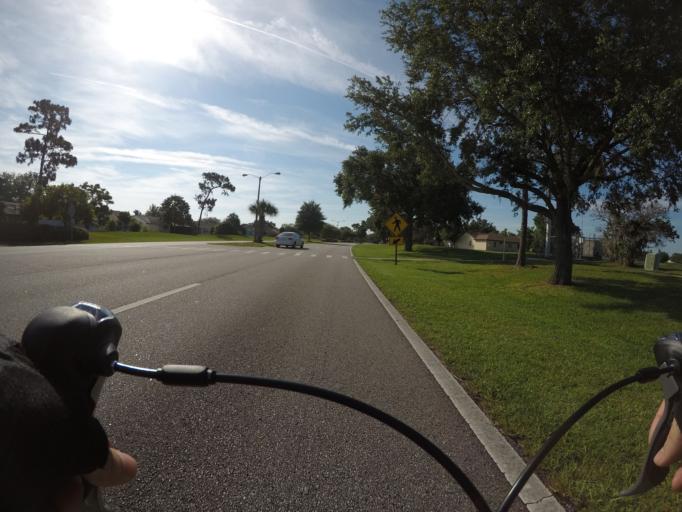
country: US
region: Florida
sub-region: Osceola County
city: Buenaventura Lakes
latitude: 28.3380
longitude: -81.3591
